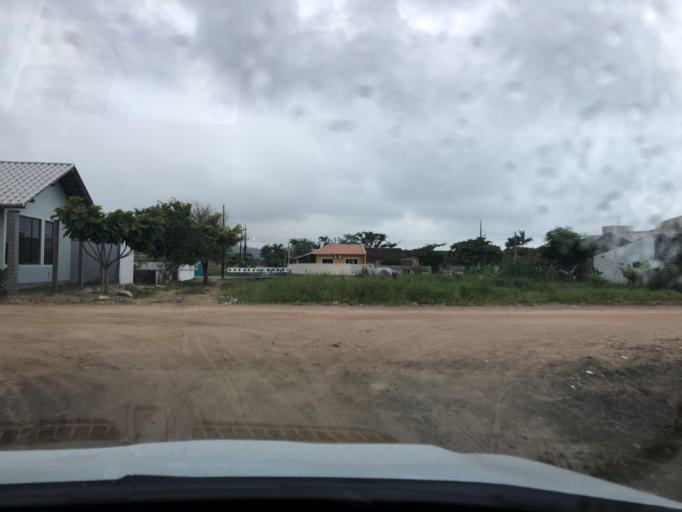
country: BR
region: Santa Catarina
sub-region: Sao Francisco Do Sul
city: Sao Francisco do Sul
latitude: -26.2220
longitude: -48.5257
